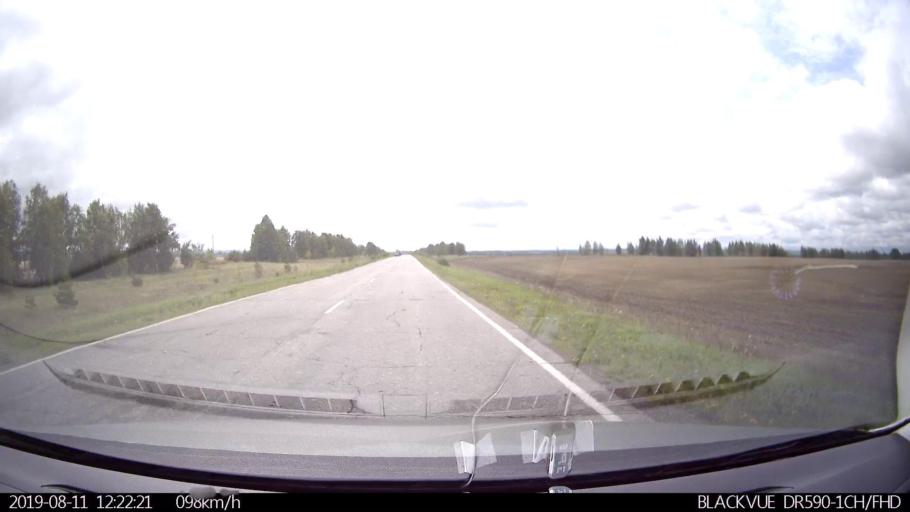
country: RU
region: Ulyanovsk
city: Ignatovka
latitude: 53.9091
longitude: 47.9551
